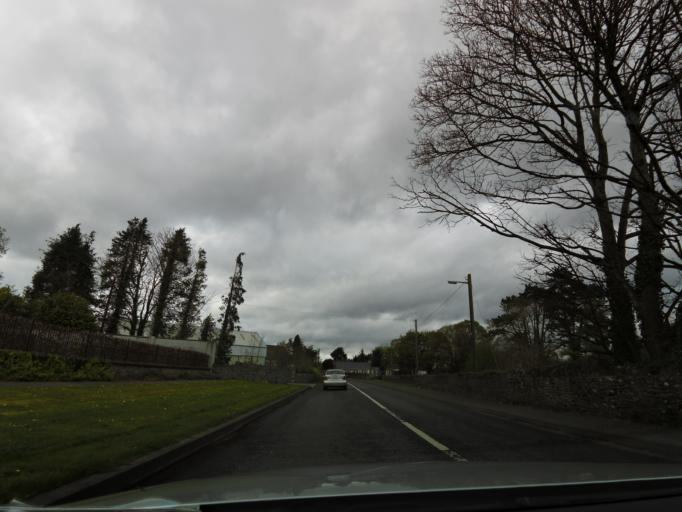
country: IE
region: Leinster
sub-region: Kilkenny
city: Kilkenny
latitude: 52.6703
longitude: -7.2668
